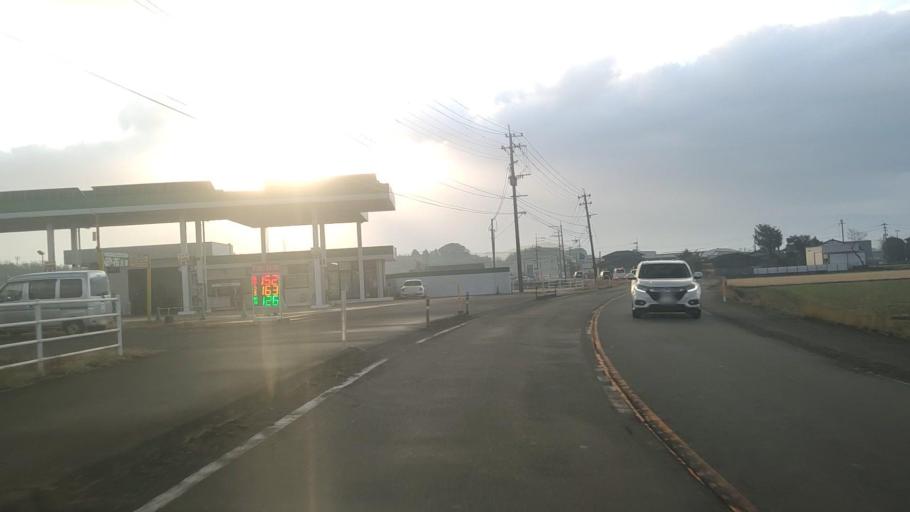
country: JP
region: Kumamoto
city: Uto
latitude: 32.7258
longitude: 130.7655
